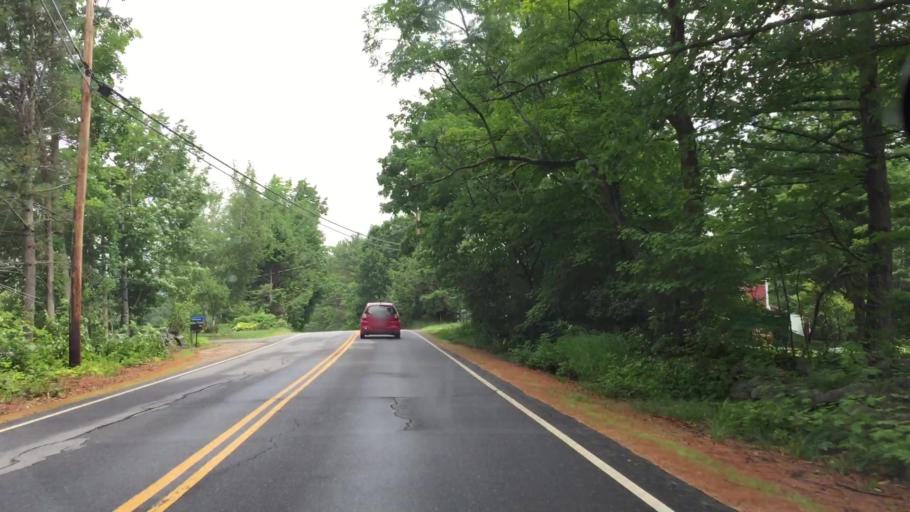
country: US
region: New Hampshire
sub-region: Carroll County
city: Sandwich
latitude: 43.7984
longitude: -71.4434
